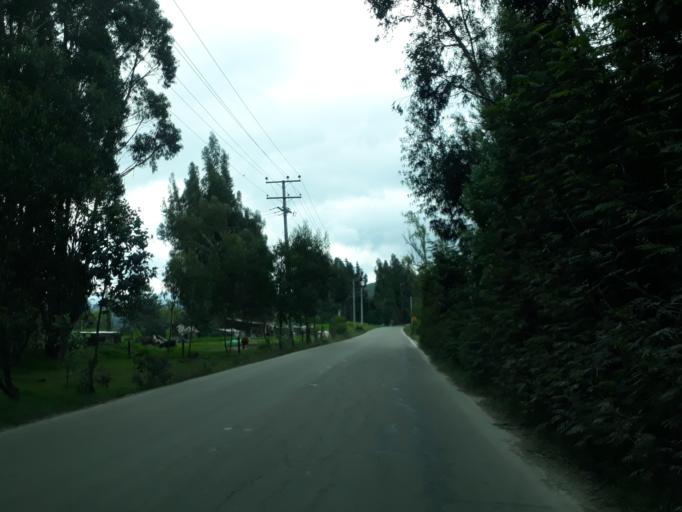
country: CO
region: Cundinamarca
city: Ubate
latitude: 5.3213
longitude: -73.7894
